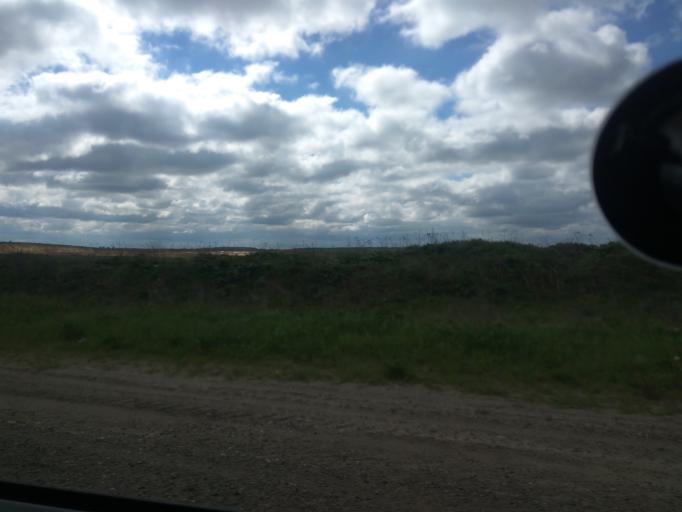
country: RU
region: Moskovskaya
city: Ostrovtsy
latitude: 55.5431
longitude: 38.0541
